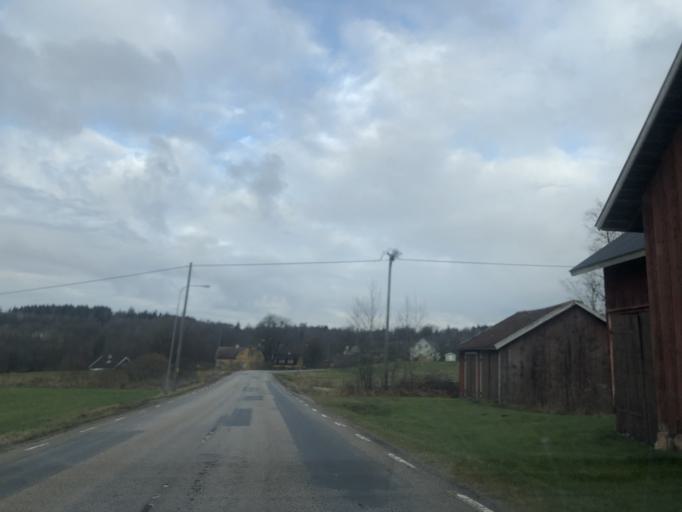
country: SE
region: Vaestra Goetaland
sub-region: Ulricehamns Kommun
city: Ulricehamn
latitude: 57.7177
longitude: 13.3006
